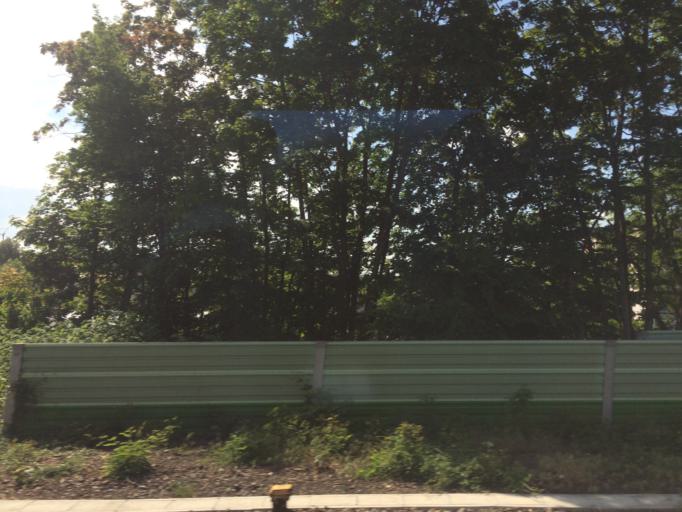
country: DE
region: Bavaria
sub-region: Regierungsbezirk Unterfranken
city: Kitzingen
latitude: 49.7368
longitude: 10.1544
